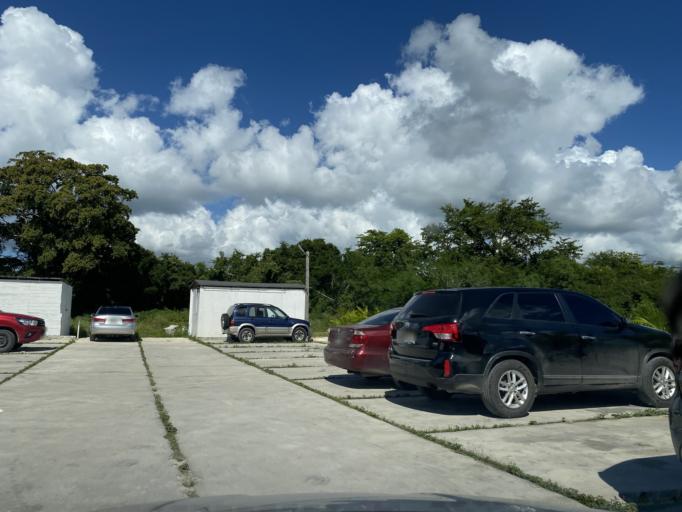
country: DO
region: La Romana
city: La Romana
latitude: 18.3528
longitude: -68.8340
